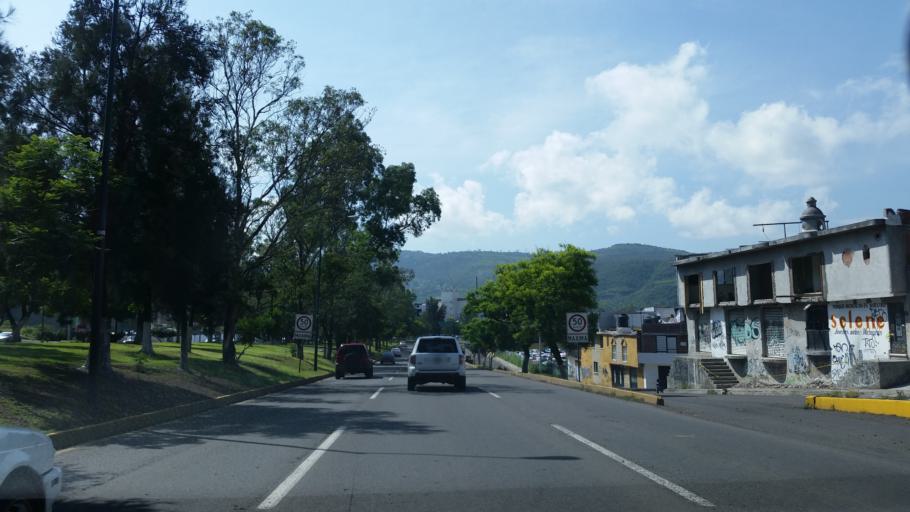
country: MX
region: Michoacan
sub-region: Morelia
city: Puerto de Buenavista (Lazaro Cardenas)
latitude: 19.6975
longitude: -101.1513
